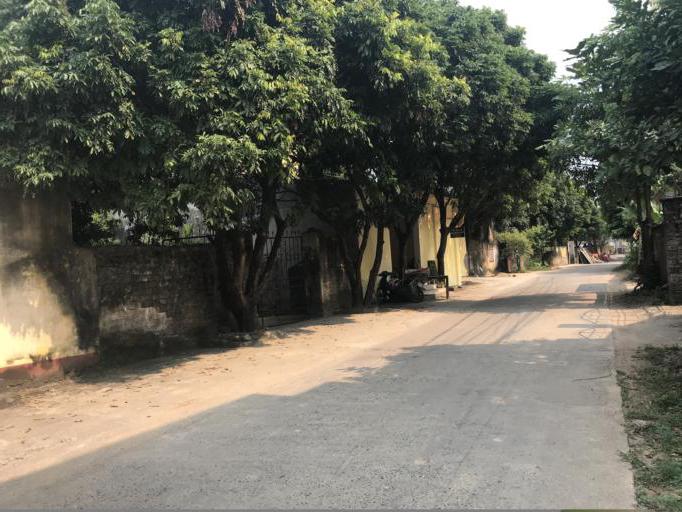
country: VN
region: Ninh Binh
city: Thanh Pho Ninh Binh
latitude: 20.2471
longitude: 105.9345
